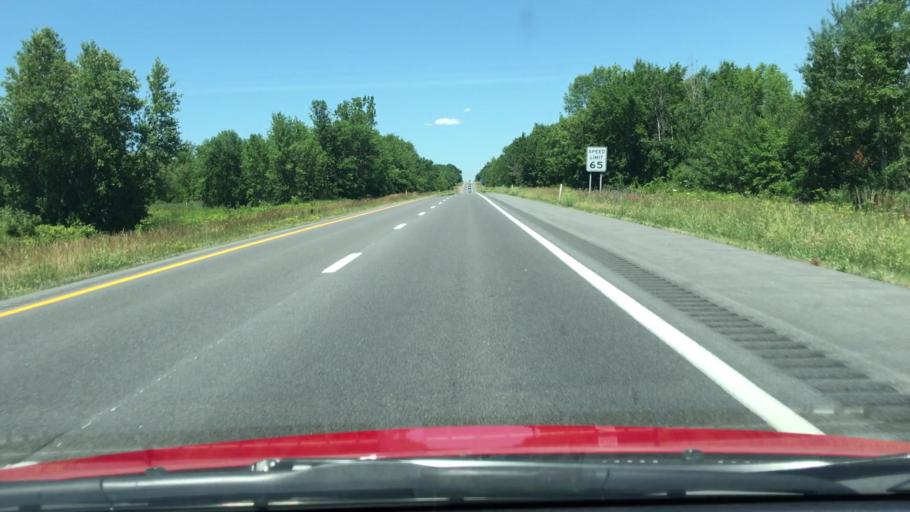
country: US
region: New York
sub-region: Clinton County
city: Cumberland Head
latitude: 44.7921
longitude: -73.4404
